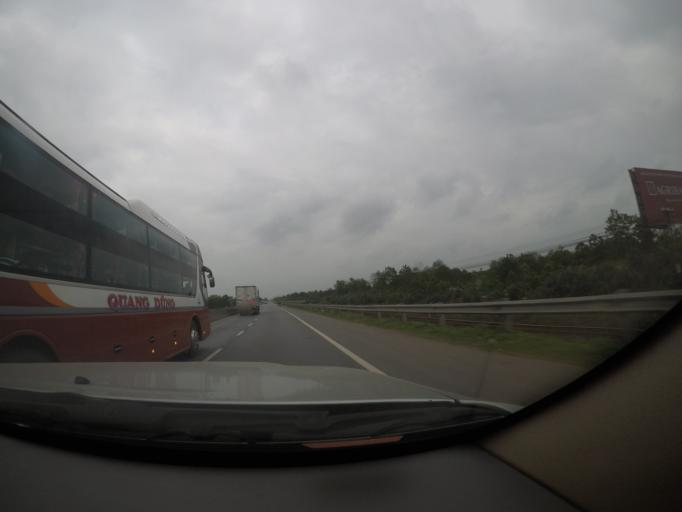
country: VN
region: Quang Tri
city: Hai Lang
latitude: 16.6540
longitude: 107.2824
